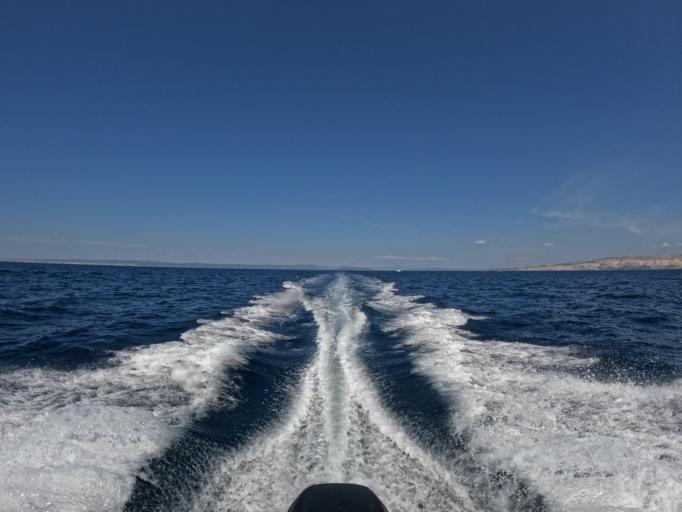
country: HR
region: Primorsko-Goranska
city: Lopar
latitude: 44.8681
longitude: 14.6749
